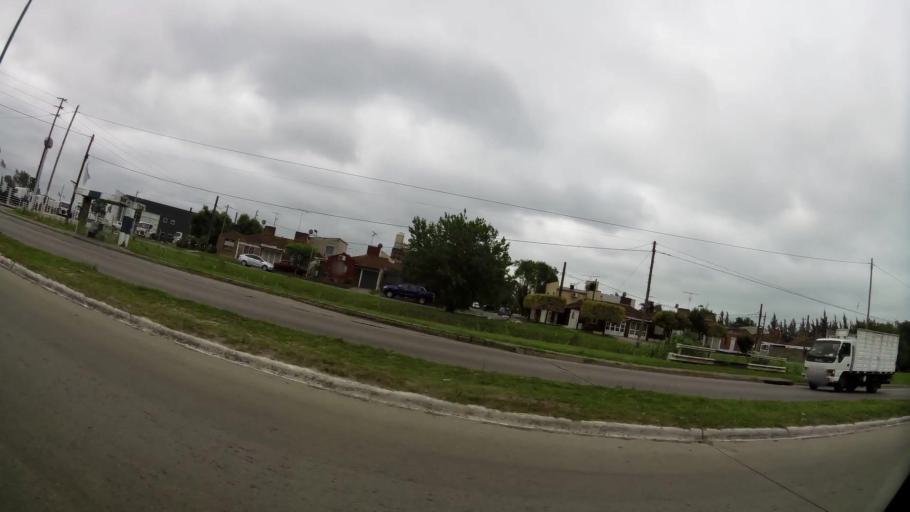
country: AR
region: Buenos Aires
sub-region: Partido de La Plata
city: La Plata
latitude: -34.9885
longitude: -58.0407
